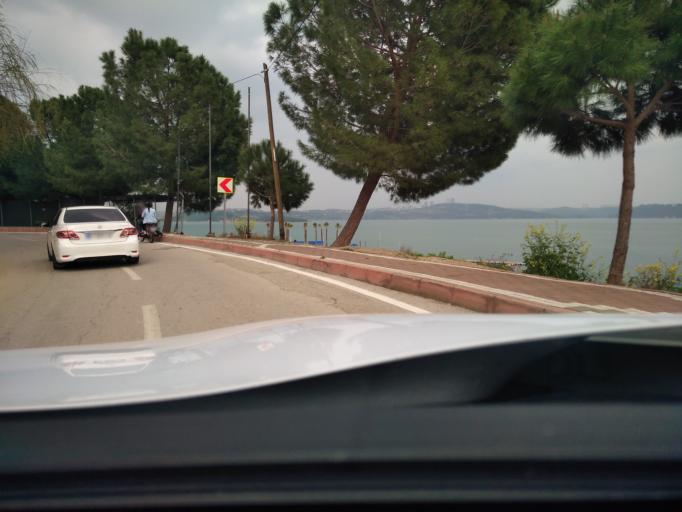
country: TR
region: Adana
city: Adana
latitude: 37.0605
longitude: 35.3022
